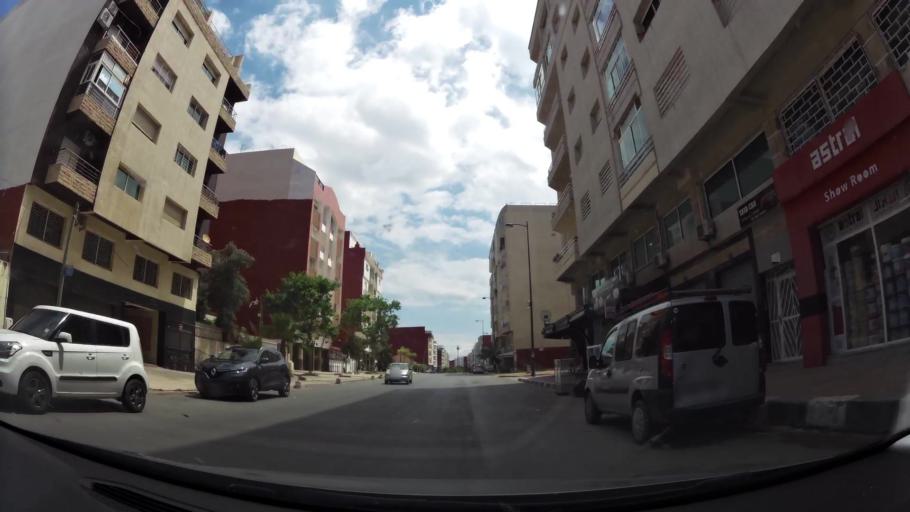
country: MA
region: Gharb-Chrarda-Beni Hssen
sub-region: Kenitra Province
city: Kenitra
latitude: 34.2586
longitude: -6.5950
